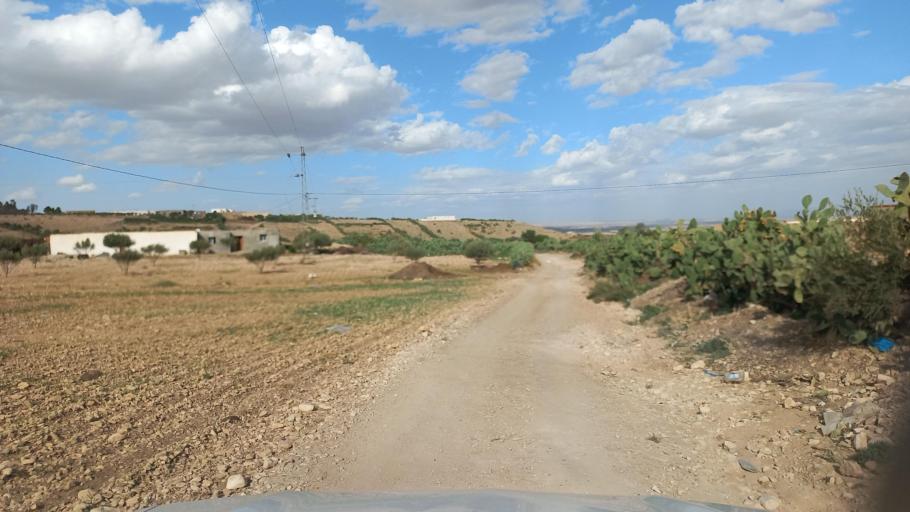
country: TN
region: Al Qasrayn
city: Sbiba
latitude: 35.4500
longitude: 9.0848
